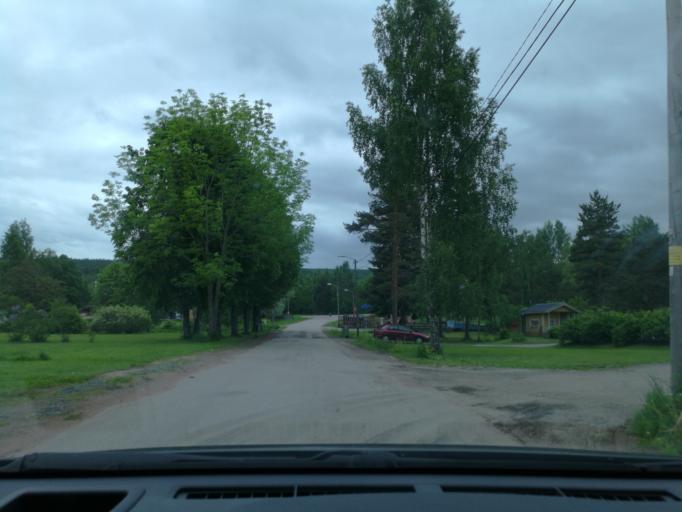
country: SE
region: Dalarna
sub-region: Smedjebackens Kommun
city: Smedjebacken
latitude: 60.1407
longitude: 15.3089
